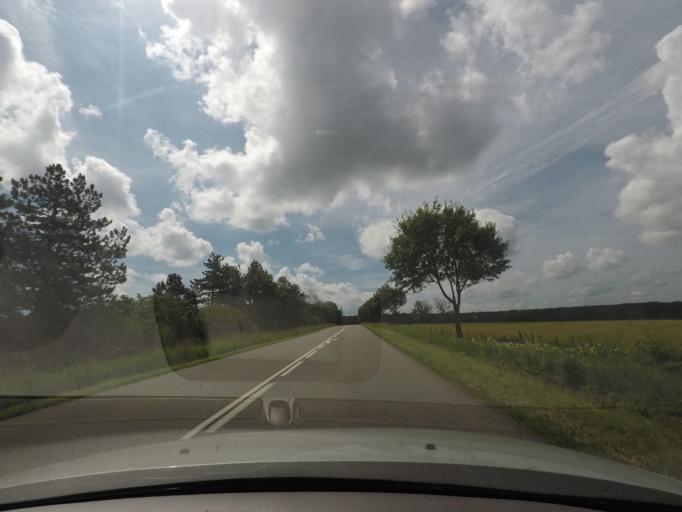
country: FR
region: Alsace
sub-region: Departement du Bas-Rhin
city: Sarrewerden
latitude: 48.8956
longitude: 7.1319
